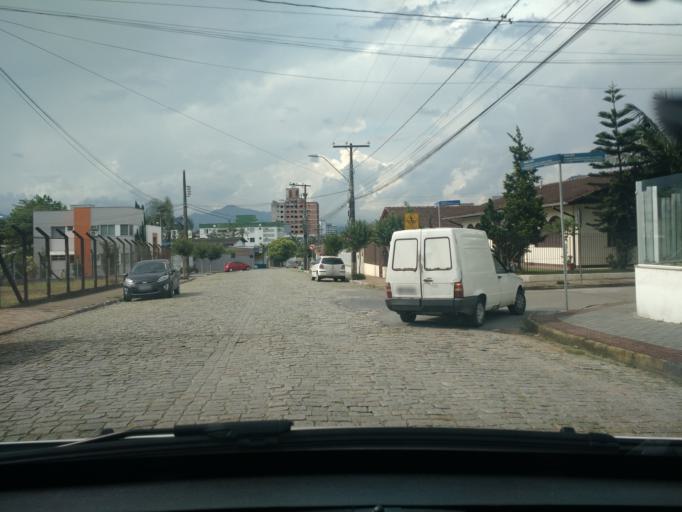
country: BR
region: Santa Catarina
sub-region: Jaragua Do Sul
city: Jaragua do Sul
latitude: -26.5053
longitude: -49.0868
